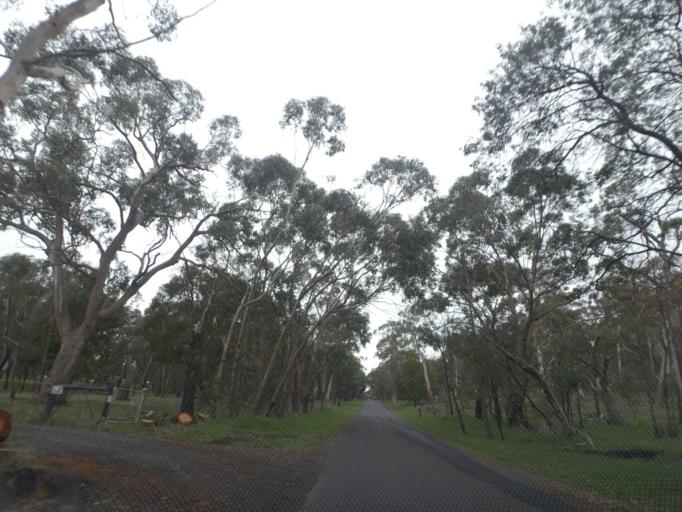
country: AU
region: Victoria
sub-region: Hume
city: Sunbury
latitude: -37.3272
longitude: 144.5915
